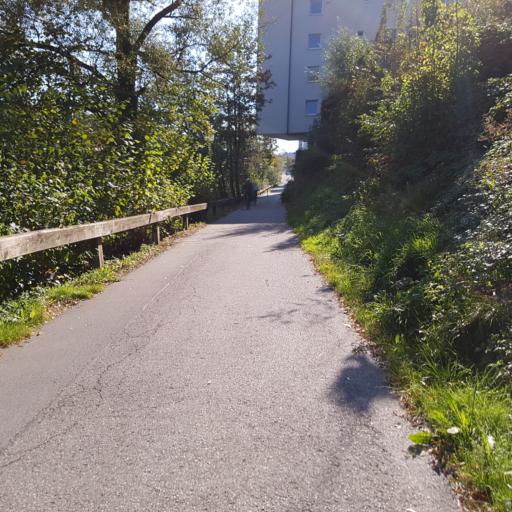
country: AT
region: Salzburg
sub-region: Politischer Bezirk Hallein
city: Hallein
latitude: 47.6865
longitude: 13.0876
